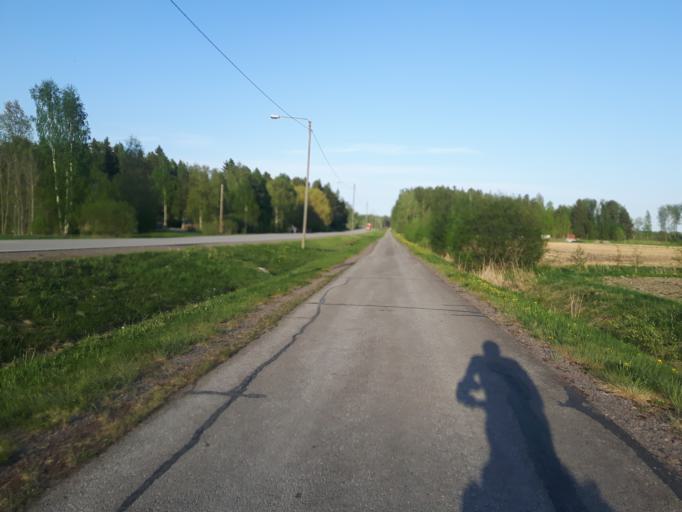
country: FI
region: Uusimaa
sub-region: Loviisa
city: Lovisa
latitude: 60.4571
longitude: 26.1289
